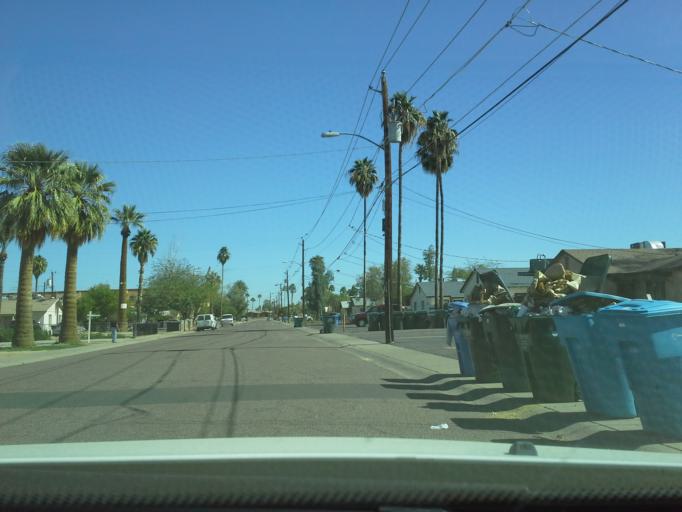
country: US
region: Arizona
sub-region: Maricopa County
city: Phoenix
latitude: 33.4999
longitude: -112.0618
